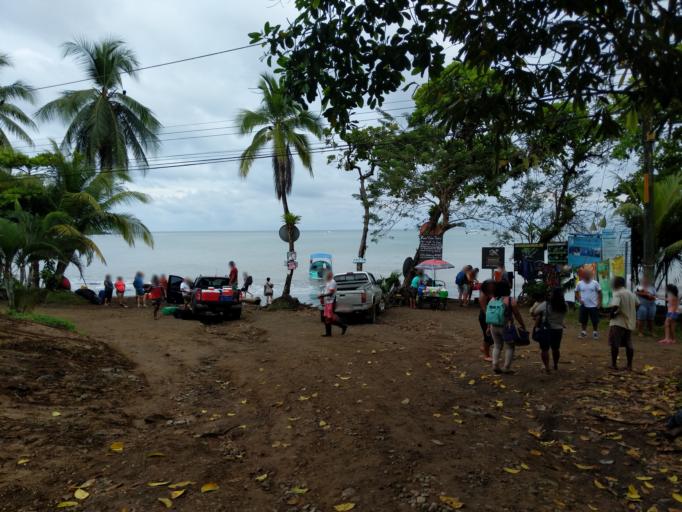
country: CR
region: Puntarenas
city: Ciudad Cortes
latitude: 8.6902
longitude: -83.6667
